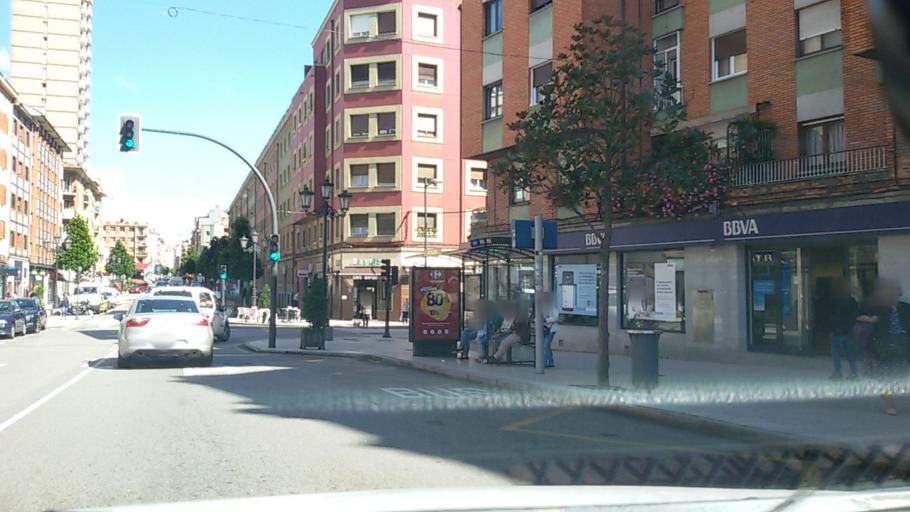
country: ES
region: Asturias
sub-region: Province of Asturias
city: Oviedo
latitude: 43.3689
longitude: -5.8388
